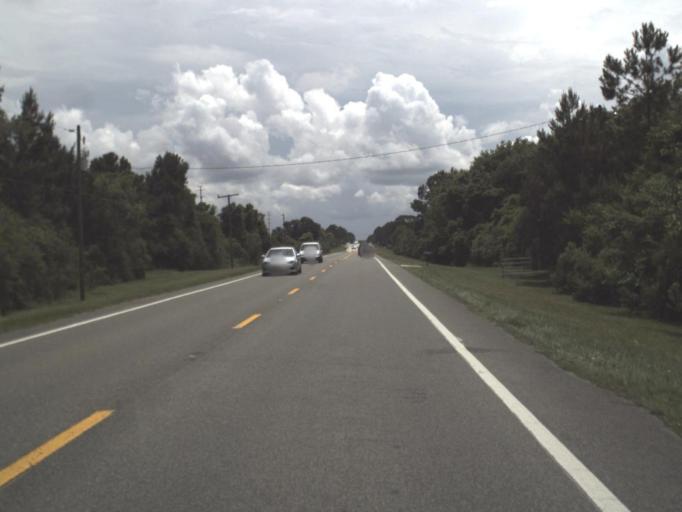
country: US
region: Florida
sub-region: Nassau County
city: Yulee
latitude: 30.5800
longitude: -81.6050
